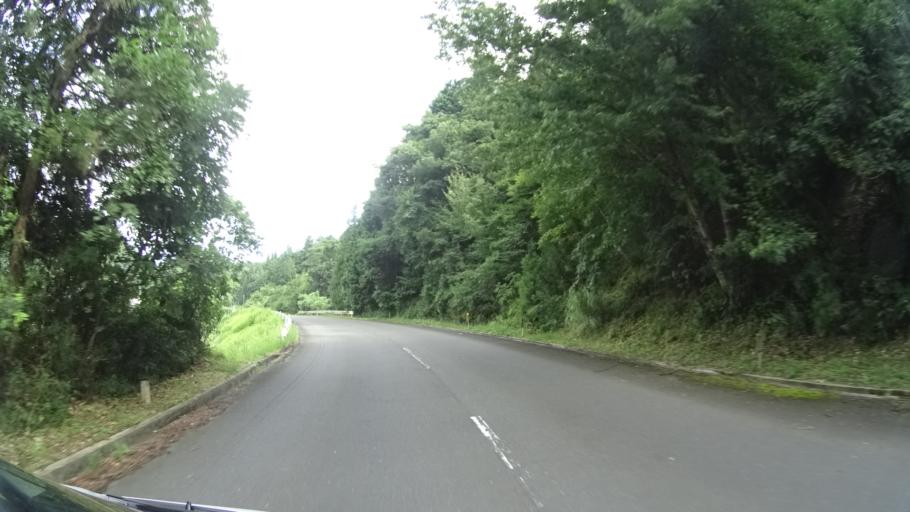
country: JP
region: Kyoto
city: Fukuchiyama
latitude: 35.3567
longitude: 135.1437
